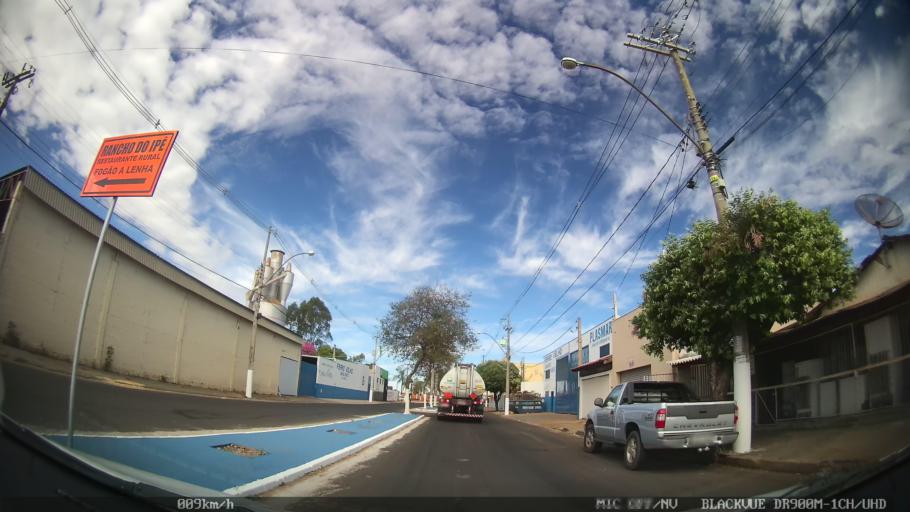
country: BR
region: Sao Paulo
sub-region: Bady Bassitt
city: Bady Bassitt
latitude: -20.8234
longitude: -49.5236
